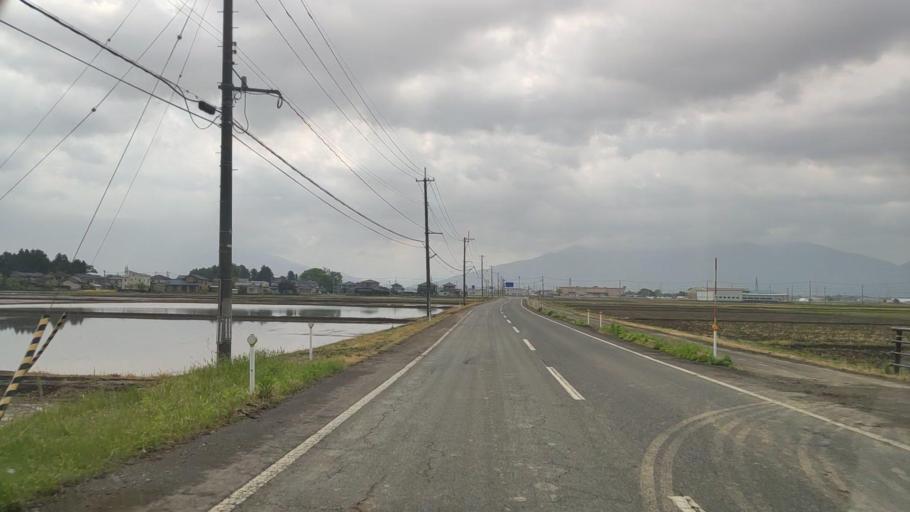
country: JP
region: Niigata
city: Gosen
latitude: 37.7293
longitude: 139.1571
